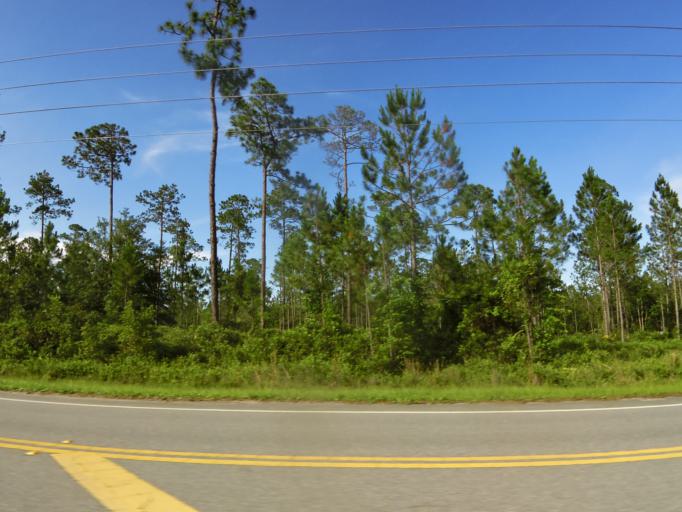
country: US
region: Florida
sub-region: Clay County
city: Green Cove Springs
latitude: 30.0036
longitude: -81.5479
